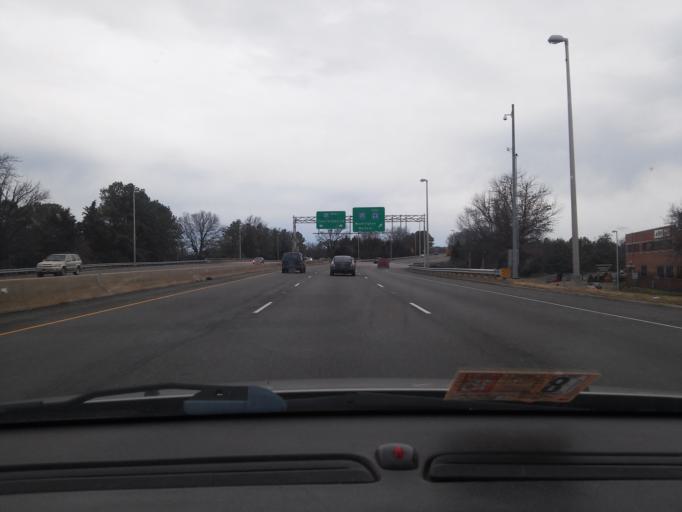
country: US
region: Virginia
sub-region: Henrico County
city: Lakeside
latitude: 37.5823
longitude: -77.4738
